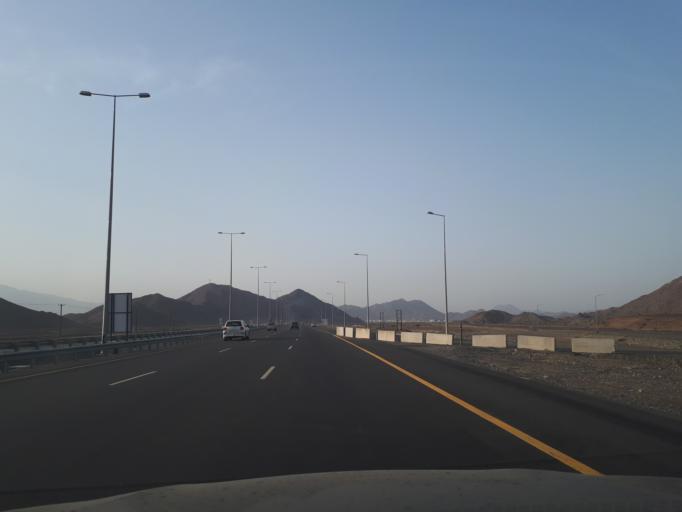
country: OM
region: Muhafazat ad Dakhiliyah
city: Sufalat Sama'il
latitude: 23.2958
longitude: 58.1105
